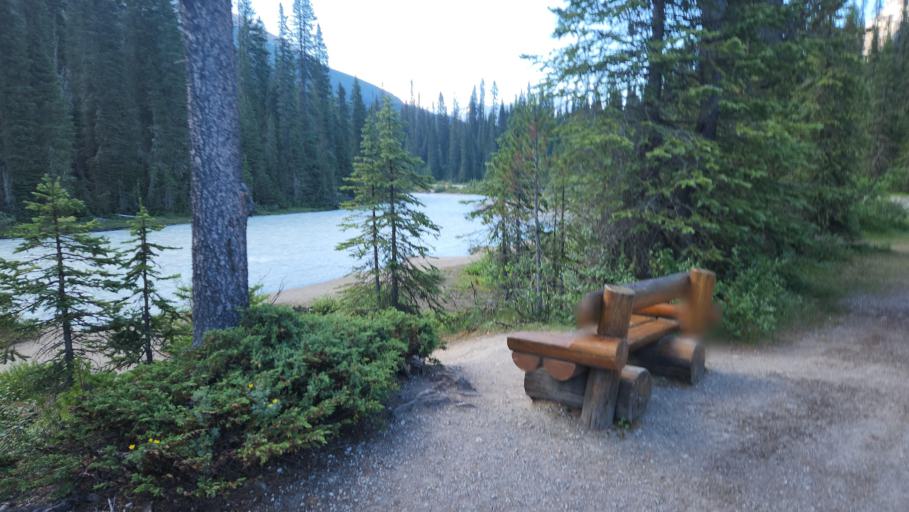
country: CA
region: Alberta
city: Lake Louise
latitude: 51.4973
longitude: -116.4827
